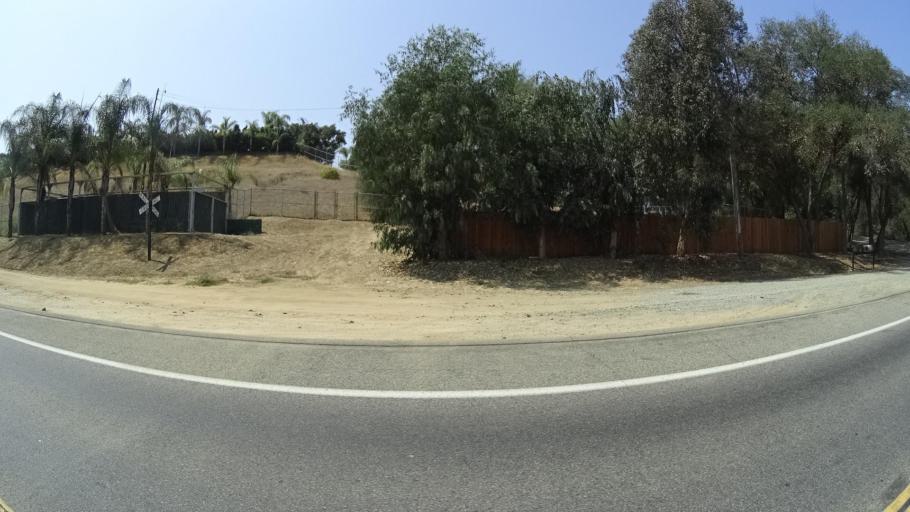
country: US
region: California
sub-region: San Diego County
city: Bonsall
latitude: 33.3187
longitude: -117.2342
